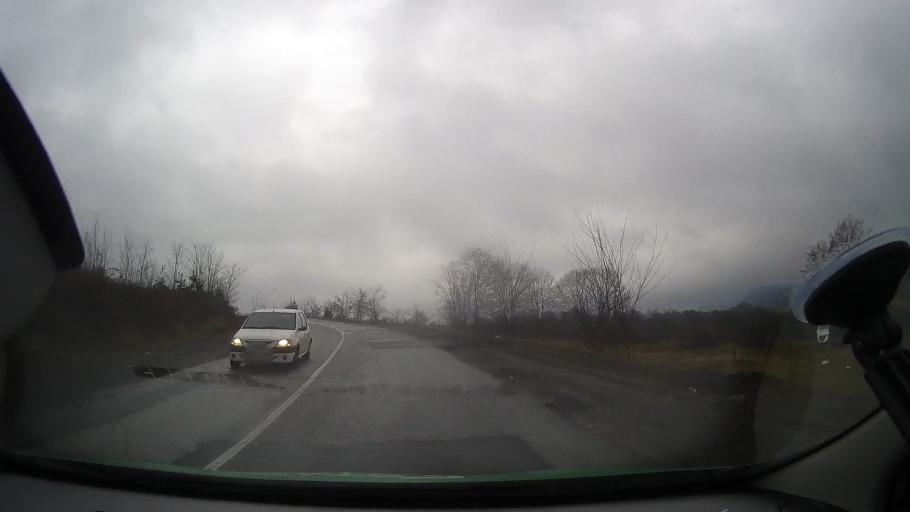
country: RO
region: Arad
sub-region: Comuna Varfurile
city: Varfurile
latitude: 46.2995
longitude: 22.5352
